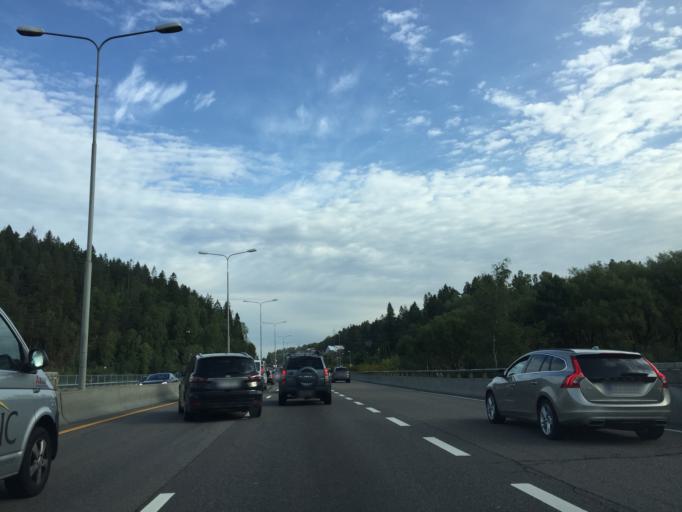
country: NO
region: Akershus
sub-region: Oppegard
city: Kolbotn
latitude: 59.8613
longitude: 10.8308
